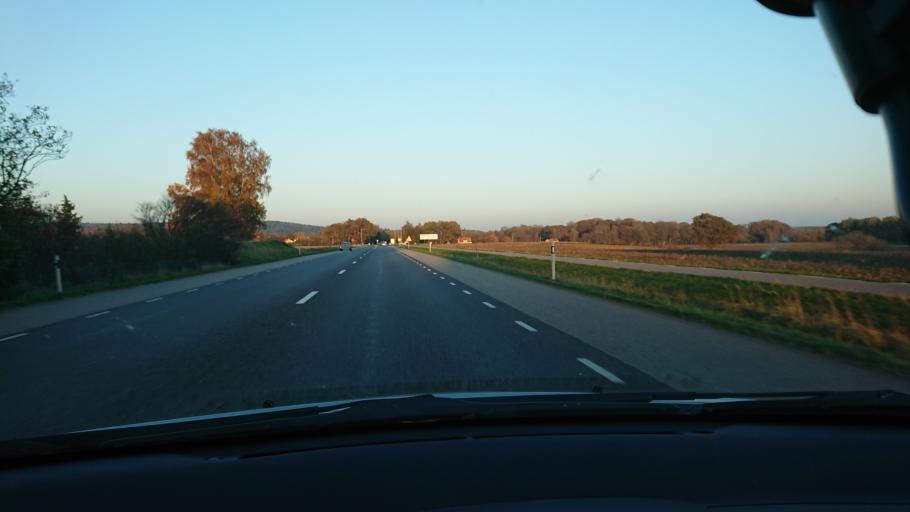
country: SE
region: Halland
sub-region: Halmstads Kommun
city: Fyllinge
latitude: 56.6910
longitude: 12.9672
